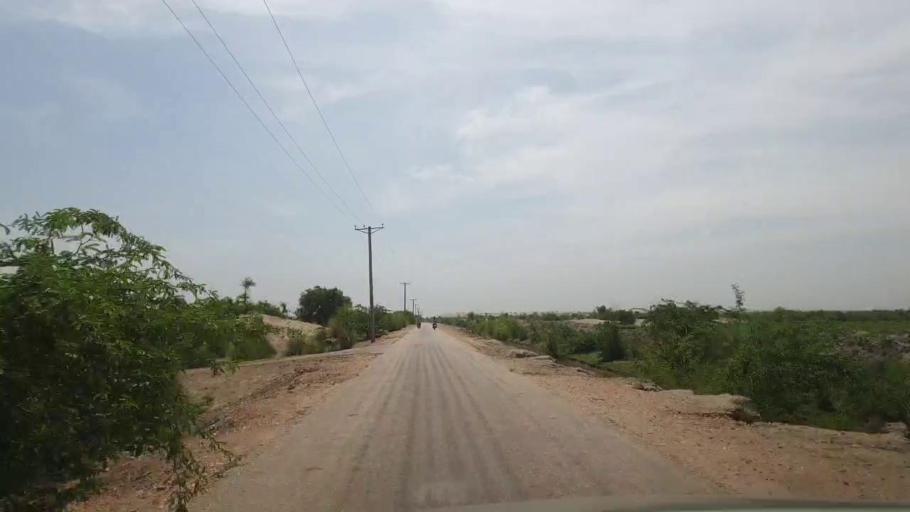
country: PK
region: Sindh
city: Kot Diji
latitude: 27.1172
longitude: 69.0087
